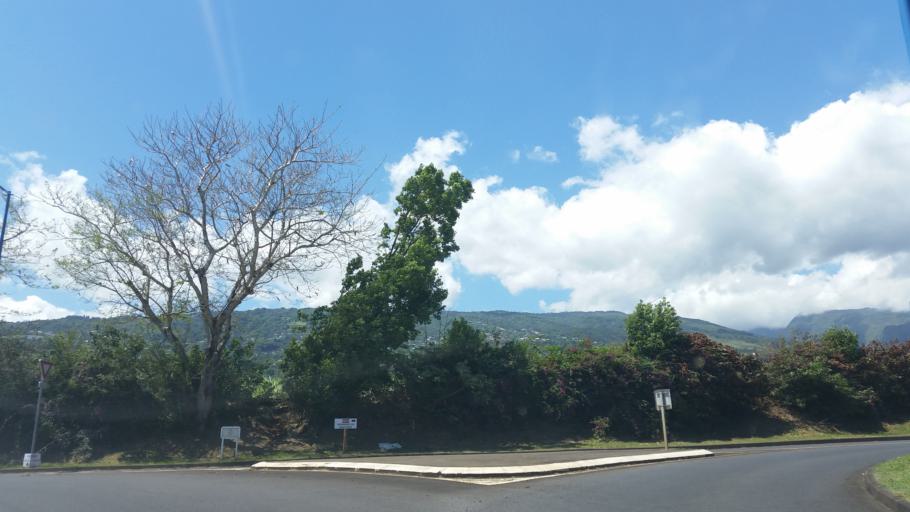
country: RE
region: Reunion
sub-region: Reunion
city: Sainte-Marie
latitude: -20.9247
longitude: 55.5298
